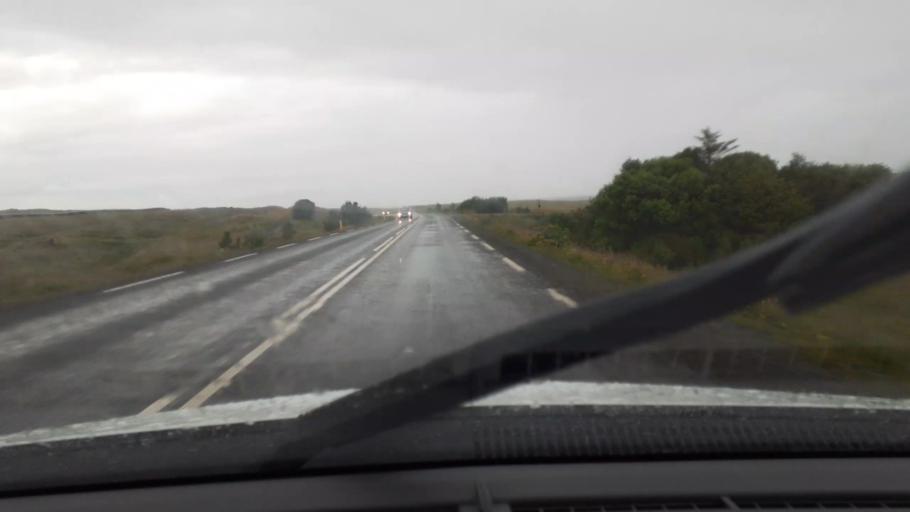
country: IS
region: West
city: Borgarnes
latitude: 64.3656
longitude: -21.9044
